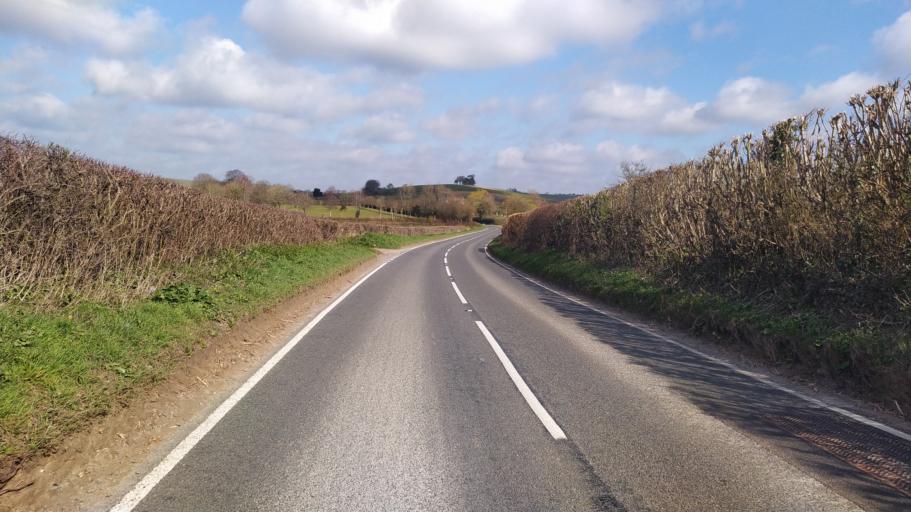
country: GB
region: England
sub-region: Dorset
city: Bridport
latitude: 50.7667
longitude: -2.7346
